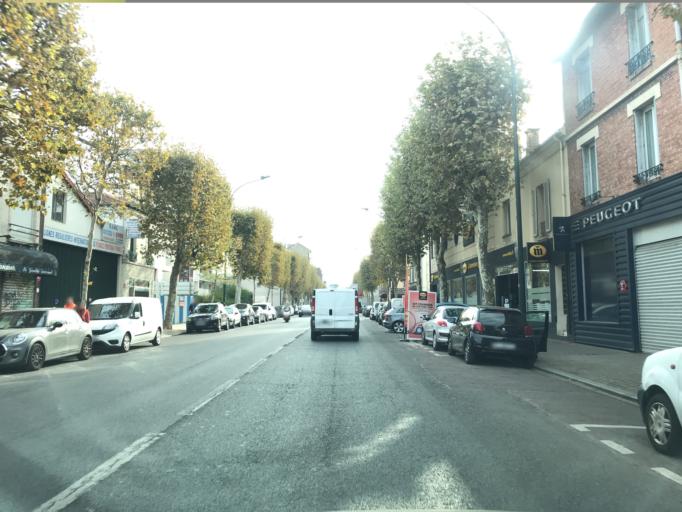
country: FR
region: Ile-de-France
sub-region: Departement des Hauts-de-Seine
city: La Garenne-Colombes
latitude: 48.9062
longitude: 2.2494
